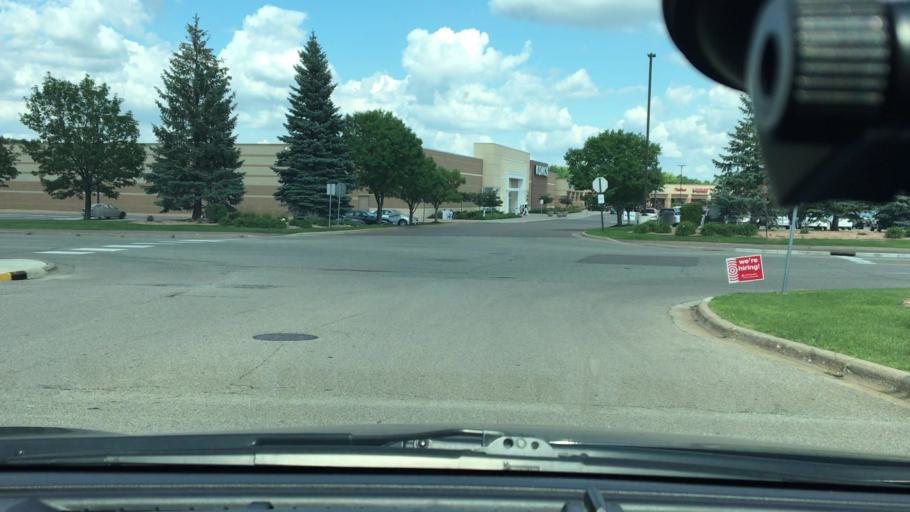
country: US
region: Minnesota
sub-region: Hennepin County
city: Plymouth
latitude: 45.0313
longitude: -93.4497
